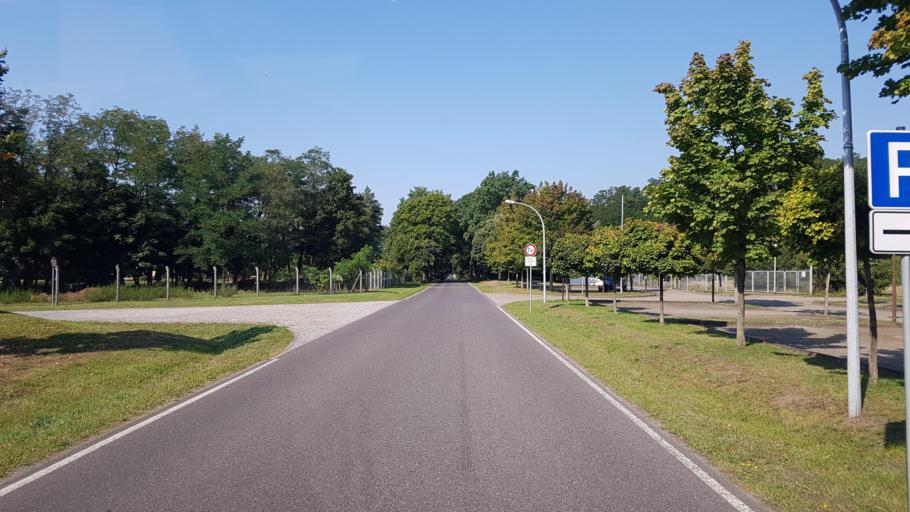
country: DE
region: Brandenburg
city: Vetschau
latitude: 51.7755
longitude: 14.0963
